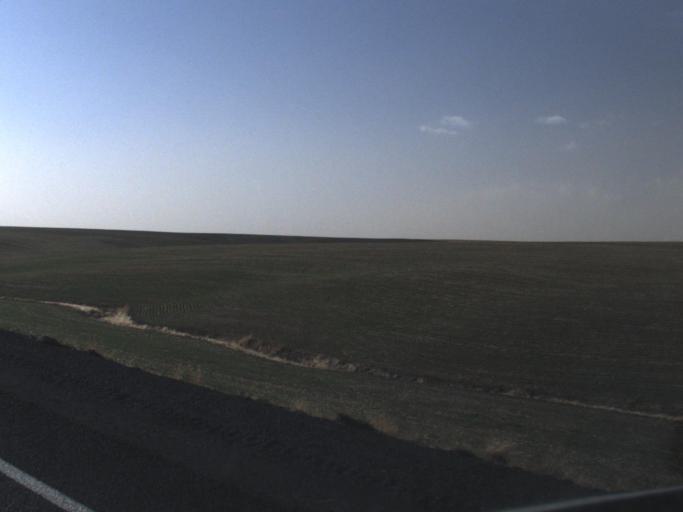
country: US
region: Washington
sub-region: Lincoln County
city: Davenport
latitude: 47.4698
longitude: -118.2927
